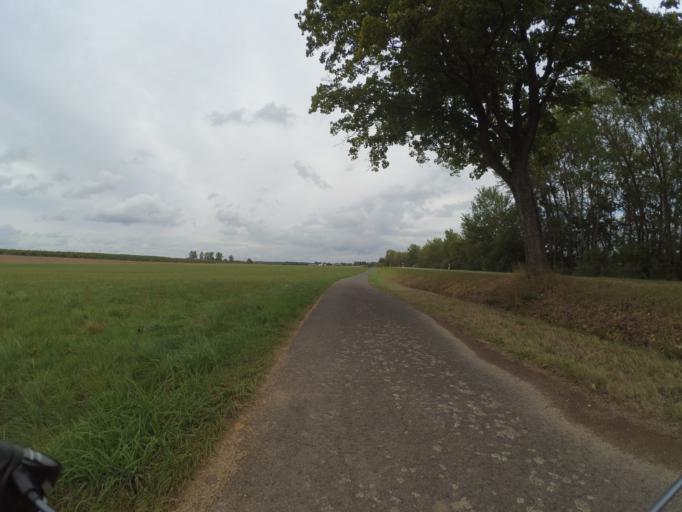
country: DE
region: Rheinland-Pfalz
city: Herforst
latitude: 49.9579
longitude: 6.6863
